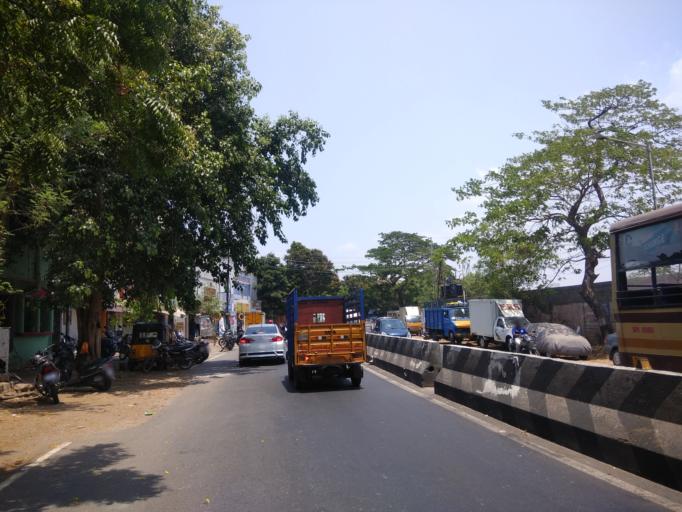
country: IN
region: Tamil Nadu
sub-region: Kancheepuram
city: Alandur
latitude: 13.0032
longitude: 80.2199
